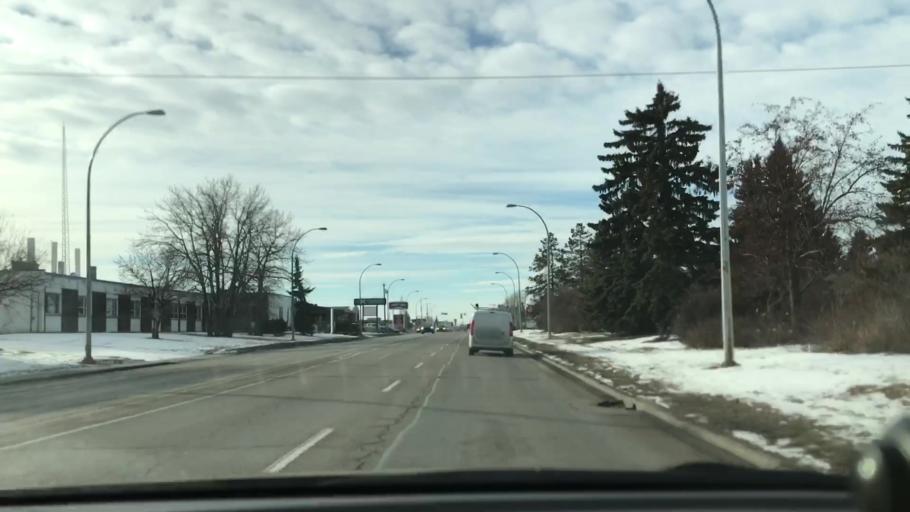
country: CA
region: Alberta
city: Edmonton
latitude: 53.5049
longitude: -113.4495
